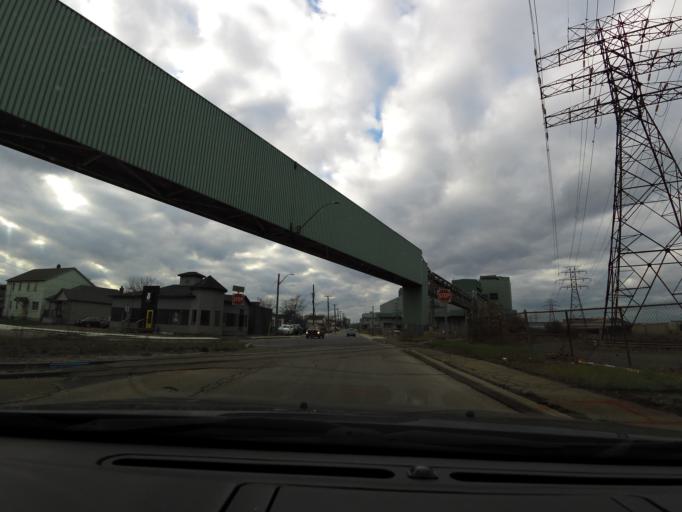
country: CA
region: Ontario
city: Hamilton
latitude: 43.2561
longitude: -79.8043
